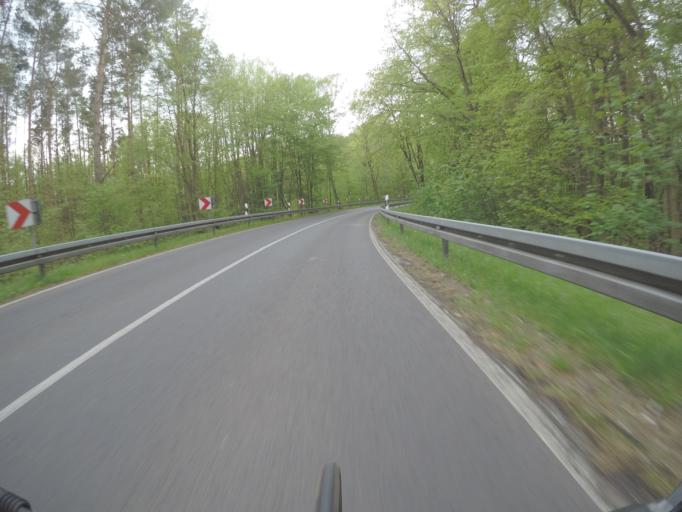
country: DE
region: Brandenburg
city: Joachimsthal
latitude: 52.9203
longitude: 13.7295
